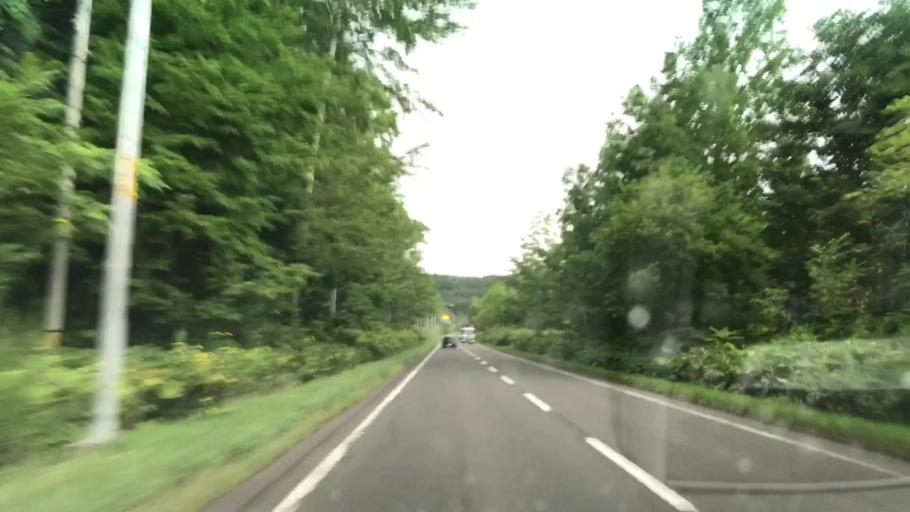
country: JP
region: Hokkaido
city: Niseko Town
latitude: 42.8245
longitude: 141.0040
